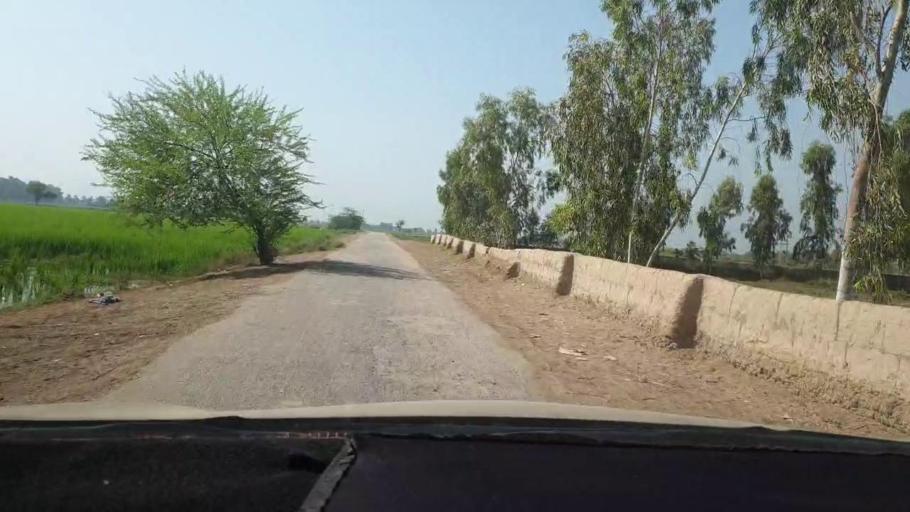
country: PK
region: Sindh
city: Miro Khan
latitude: 27.7326
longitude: 68.1185
